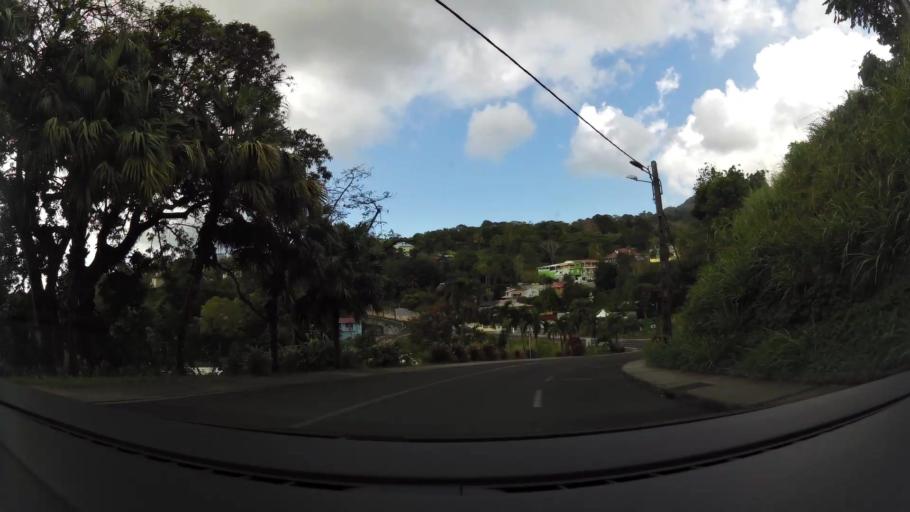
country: GP
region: Guadeloupe
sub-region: Guadeloupe
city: Trois-Rivieres
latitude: 15.9778
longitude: -61.6436
